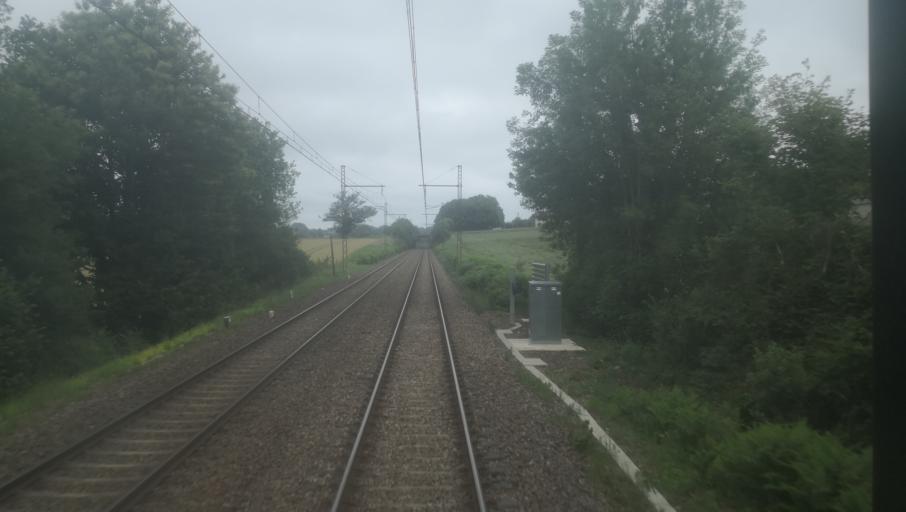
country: FR
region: Limousin
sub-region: Departement de la Creuse
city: La Souterraine
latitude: 46.2039
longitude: 1.4768
